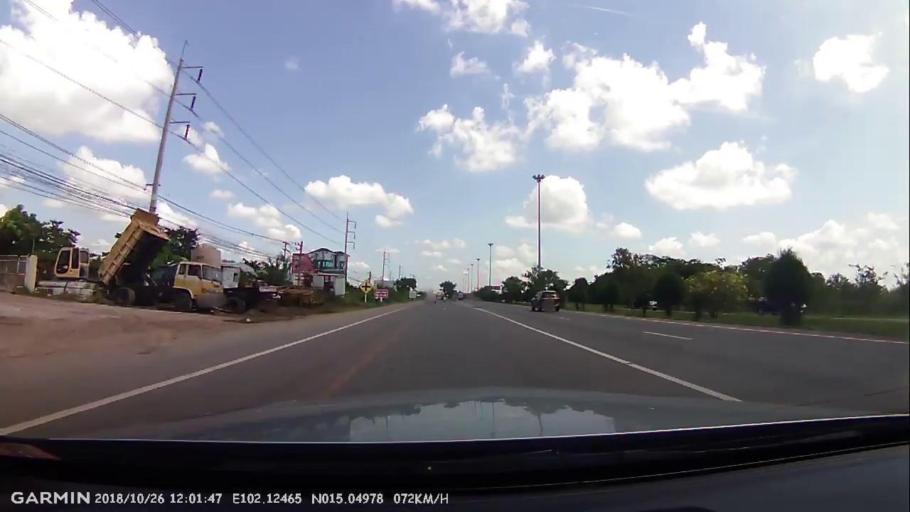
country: TH
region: Nakhon Ratchasima
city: Nakhon Ratchasima
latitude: 15.0498
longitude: 102.1247
